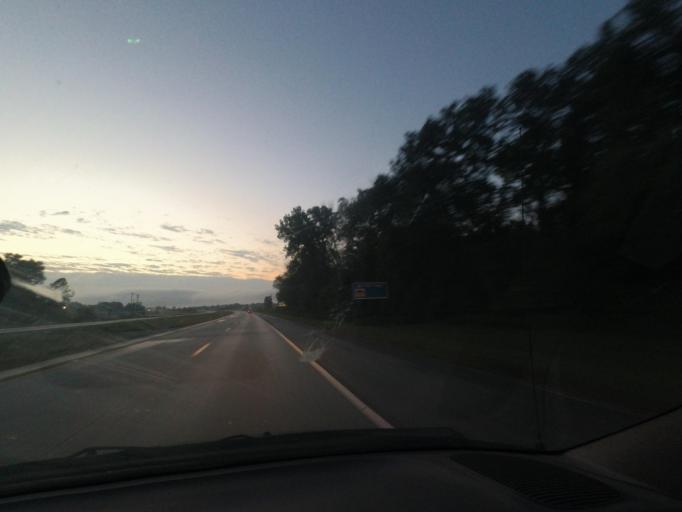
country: US
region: Missouri
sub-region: Linn County
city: Brookfield
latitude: 39.7737
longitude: -93.0836
